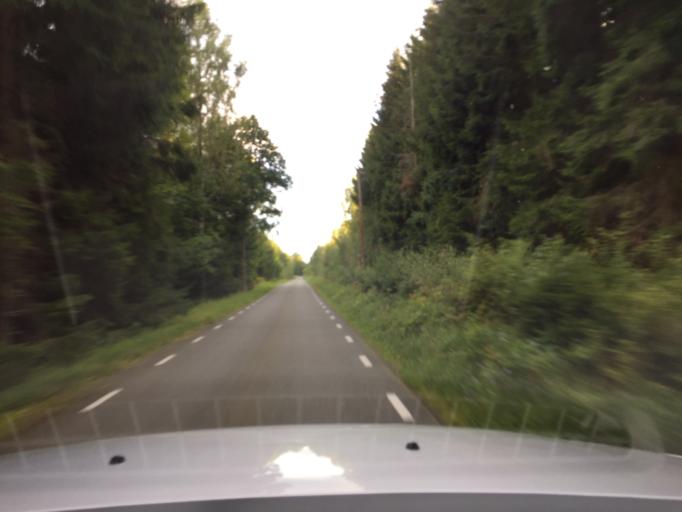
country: SE
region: Skane
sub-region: Hassleholms Kommun
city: Sosdala
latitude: 56.0222
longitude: 13.7407
